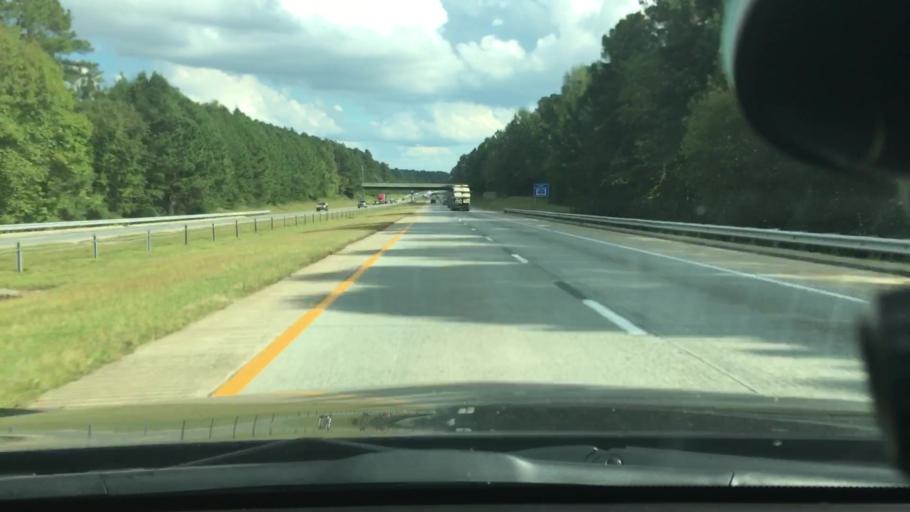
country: US
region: North Carolina
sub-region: Orange County
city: Chapel Hill
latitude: 35.9618
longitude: -79.0161
